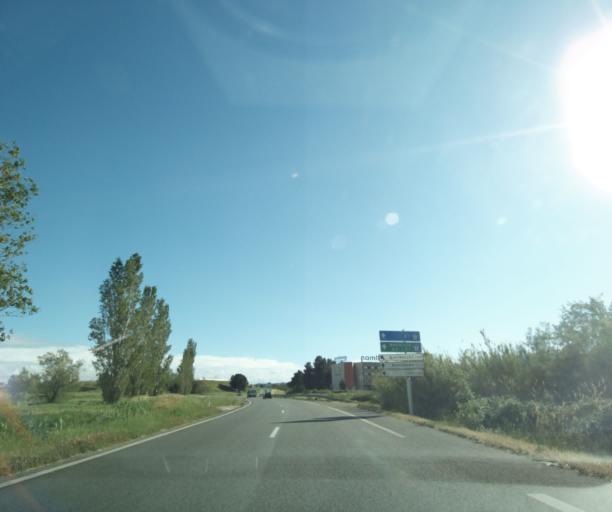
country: FR
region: Provence-Alpes-Cote d'Azur
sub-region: Departement des Bouches-du-Rhone
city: Vitrolles
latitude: 43.4479
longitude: 5.2298
